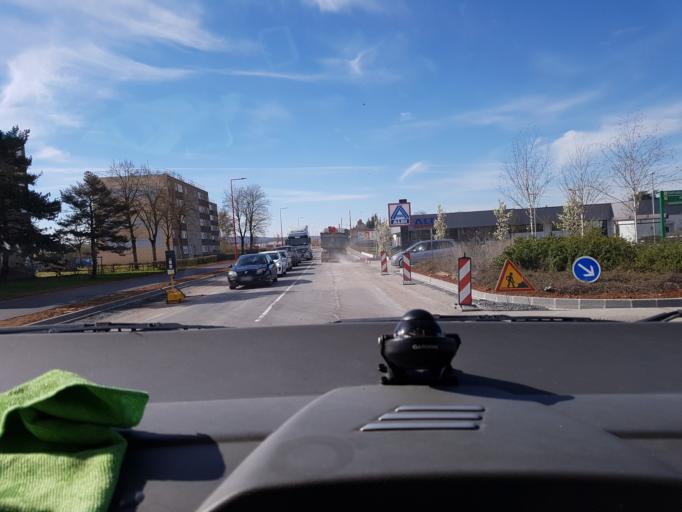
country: FR
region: Bourgogne
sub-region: Departement de Saone-et-Loire
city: Gueugnon
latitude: 46.5941
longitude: 4.0663
